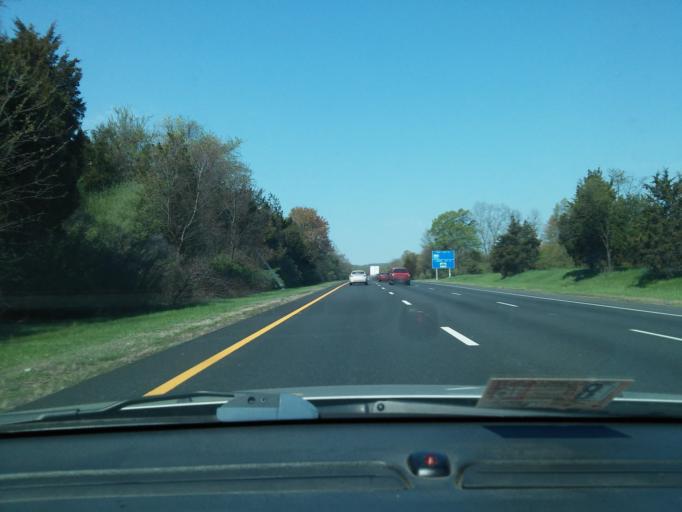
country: US
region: New Jersey
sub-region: Somerset County
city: Martinsville
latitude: 40.6463
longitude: -74.5547
